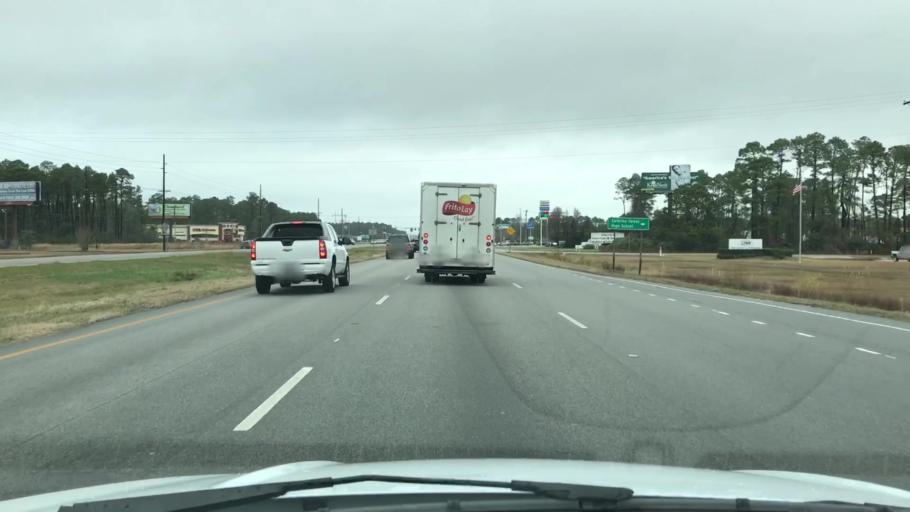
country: US
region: South Carolina
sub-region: Horry County
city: Forestbrook
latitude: 33.7731
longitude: -78.9808
